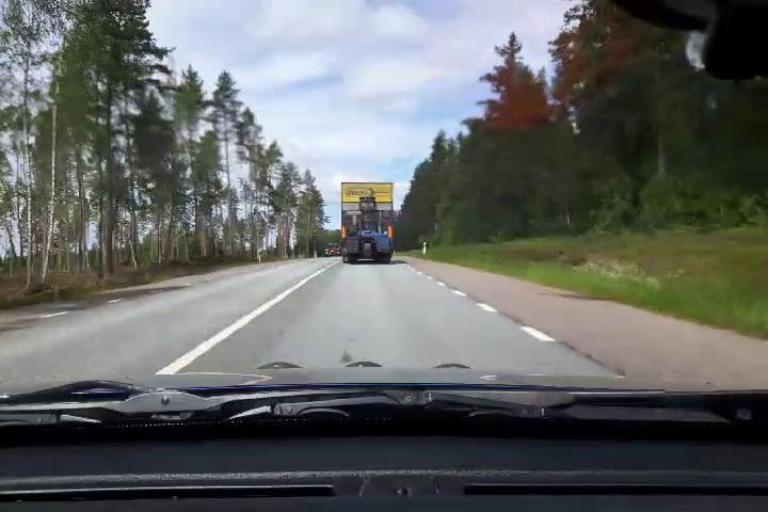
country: SE
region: Uppsala
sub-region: Tierps Kommun
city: Tierp
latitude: 60.2075
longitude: 17.4823
